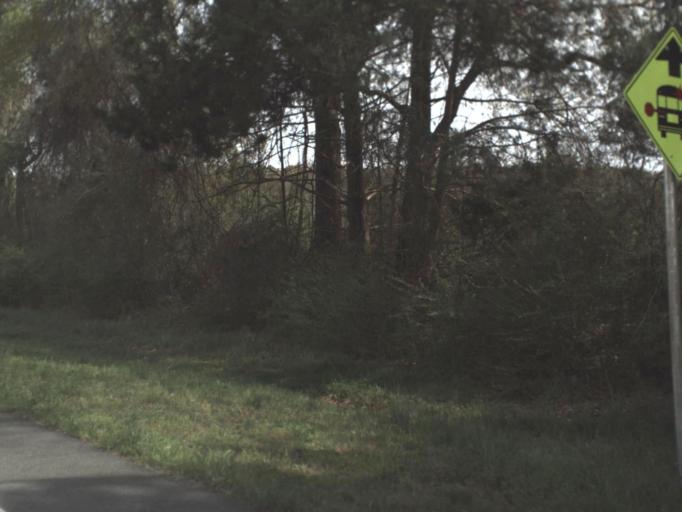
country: US
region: Alabama
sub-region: Houston County
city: Cottonwood
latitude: 30.9366
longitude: -85.3187
